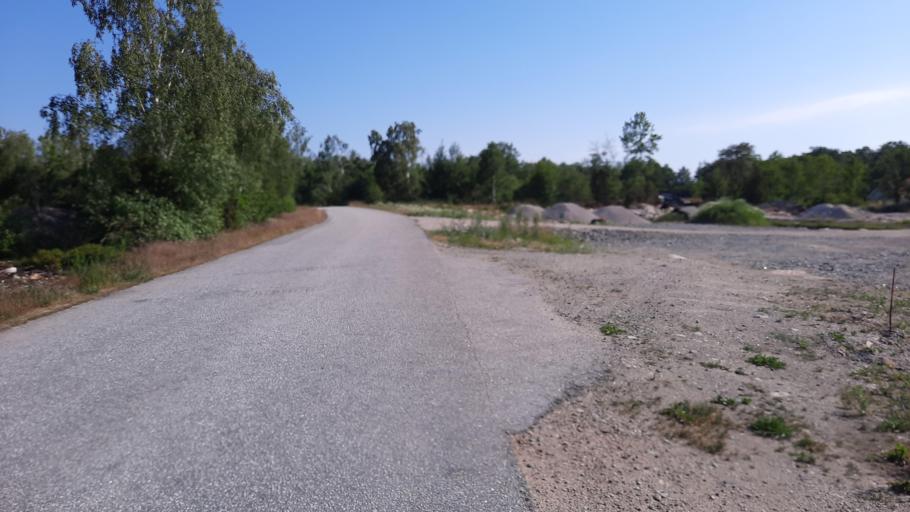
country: SE
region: Blekinge
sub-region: Karlskrona Kommun
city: Sturko
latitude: 56.1177
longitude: 15.6595
